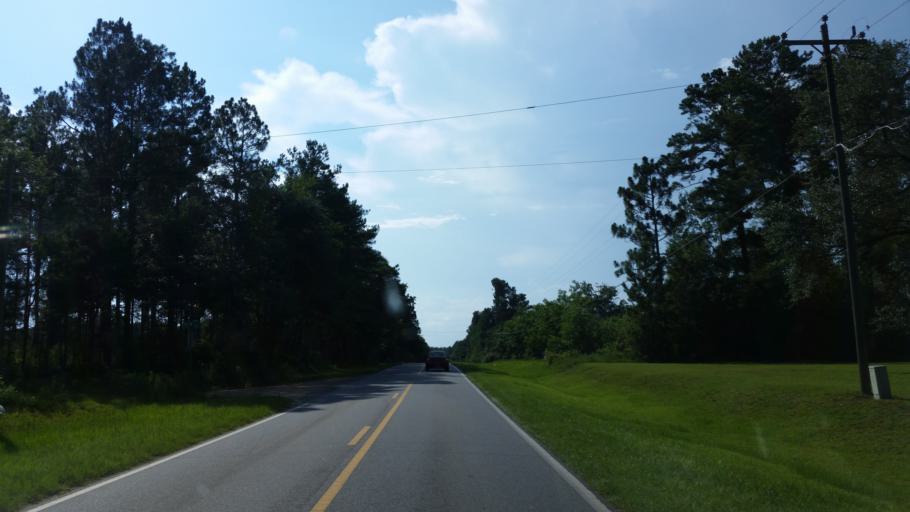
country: US
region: Georgia
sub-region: Lowndes County
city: Hahira
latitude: 30.9273
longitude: -83.3982
